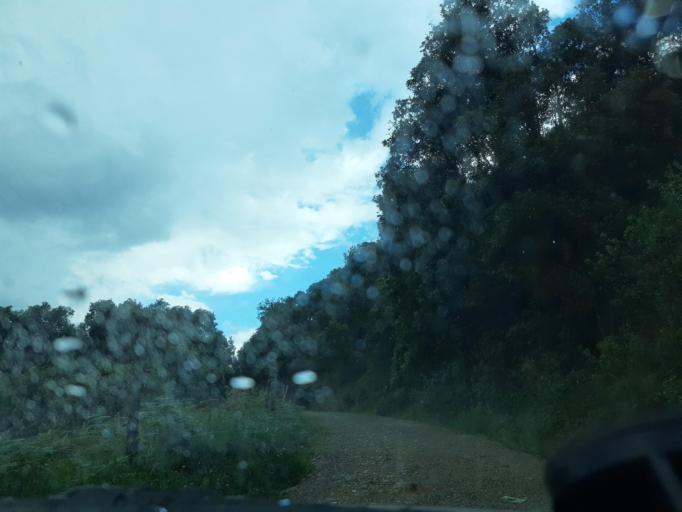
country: CO
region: Boyaca
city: Raquira
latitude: 5.5031
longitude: -73.6892
